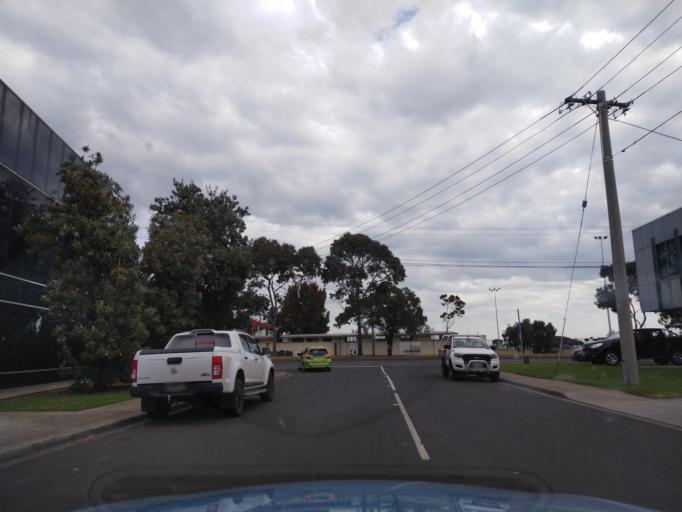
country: AU
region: Victoria
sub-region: Hobsons Bay
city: Williamstown North
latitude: -37.8549
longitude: 144.8651
